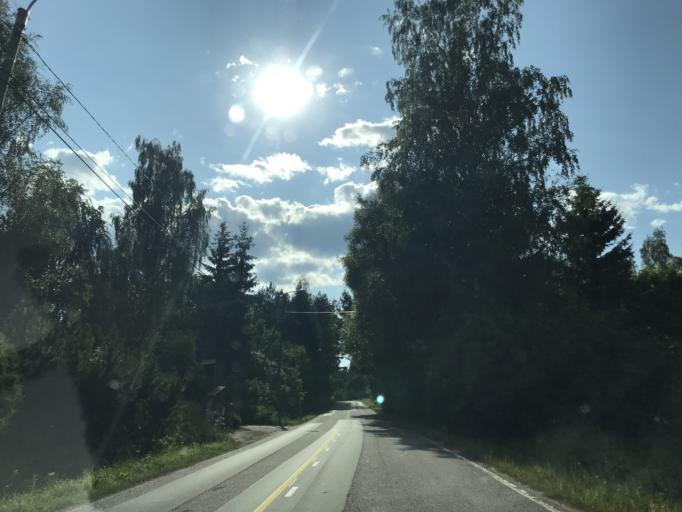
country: FI
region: Uusimaa
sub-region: Helsinki
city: Nurmijaervi
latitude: 60.4513
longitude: 24.5863
